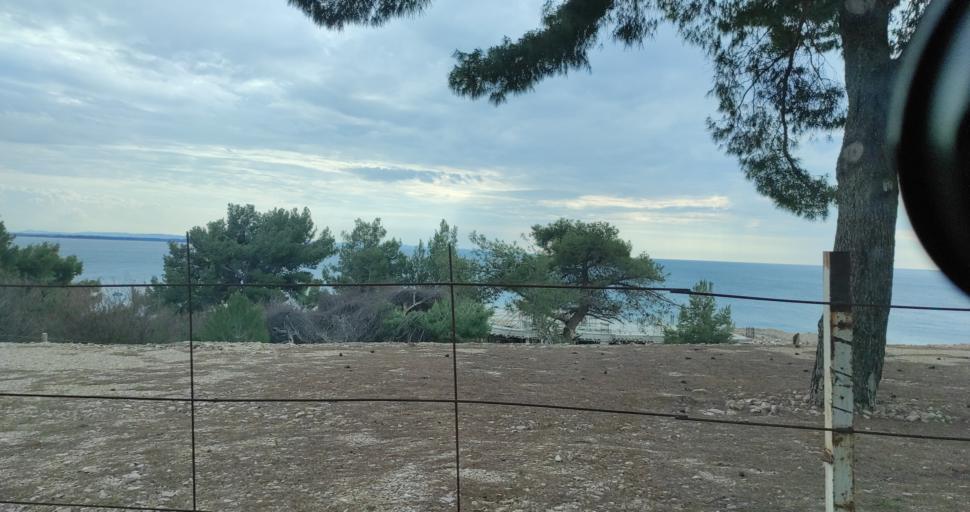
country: AL
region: Lezhe
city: Shengjin
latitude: 41.8112
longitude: 19.5816
